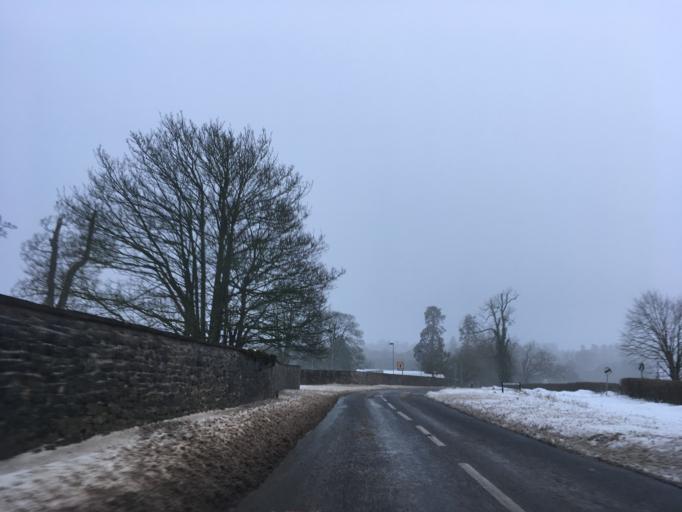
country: GB
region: England
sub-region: South Gloucestershire
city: Falfield
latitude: 51.6257
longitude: -2.4368
